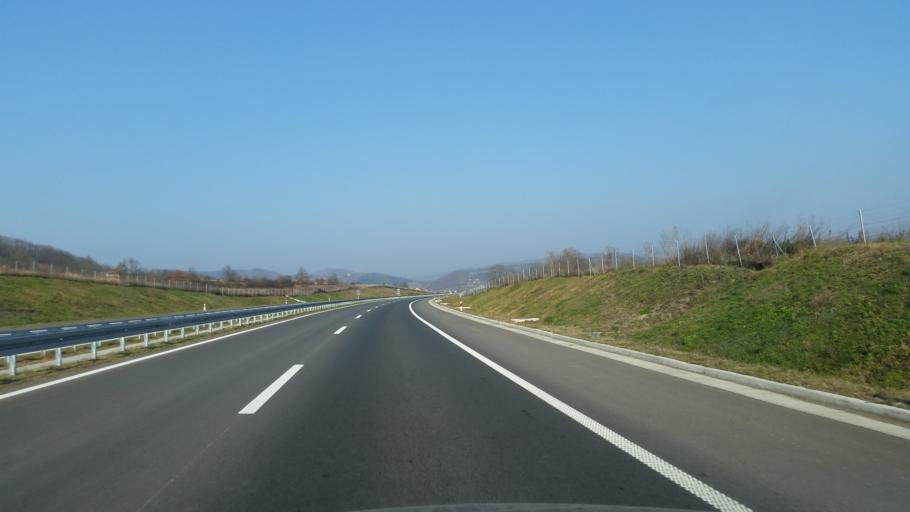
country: RS
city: Prislonica
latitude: 43.9426
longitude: 20.4003
